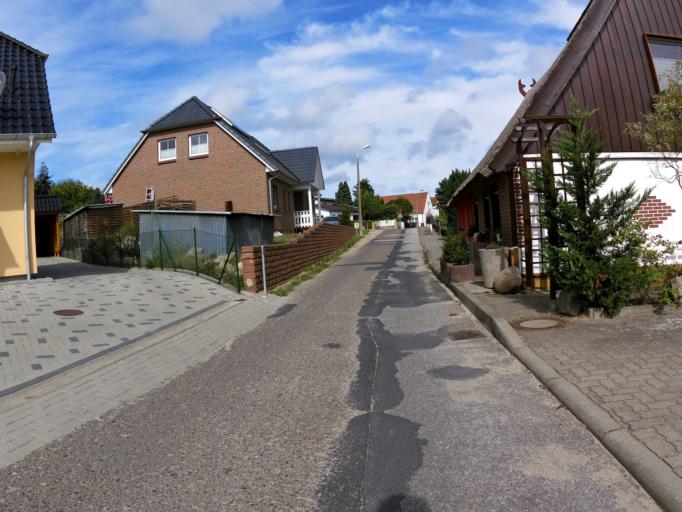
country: DE
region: Mecklenburg-Vorpommern
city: Seebad Bansin
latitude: 53.9583
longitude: 14.1288
